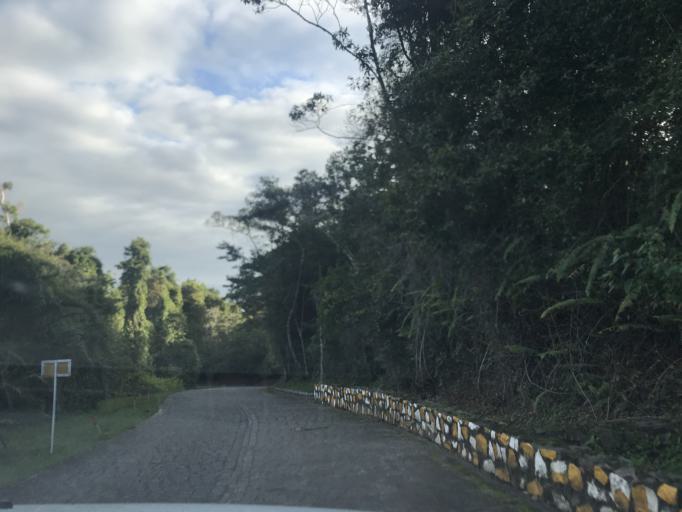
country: BR
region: Bahia
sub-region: Gandu
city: Gandu
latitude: -13.9018
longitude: -39.4611
